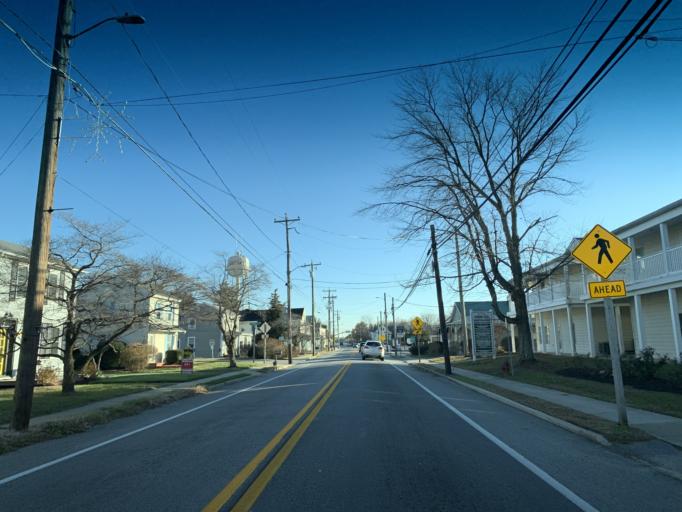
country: US
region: Delaware
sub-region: New Castle County
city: Townsend
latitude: 39.3426
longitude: -75.8793
